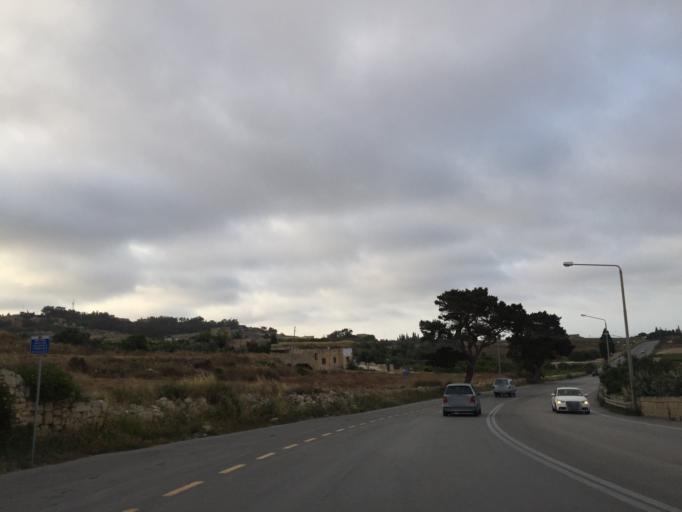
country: MT
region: L-Imdina
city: Imdina
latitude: 35.8866
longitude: 14.4071
